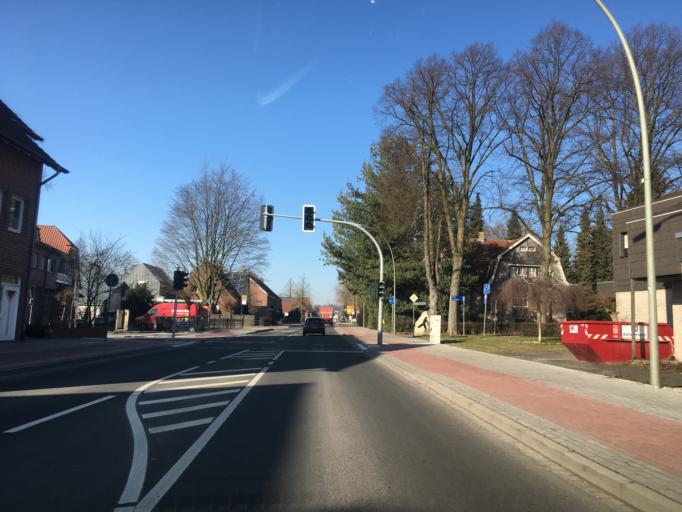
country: DE
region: North Rhine-Westphalia
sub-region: Regierungsbezirk Munster
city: Billerbeck
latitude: 51.9800
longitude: 7.2950
